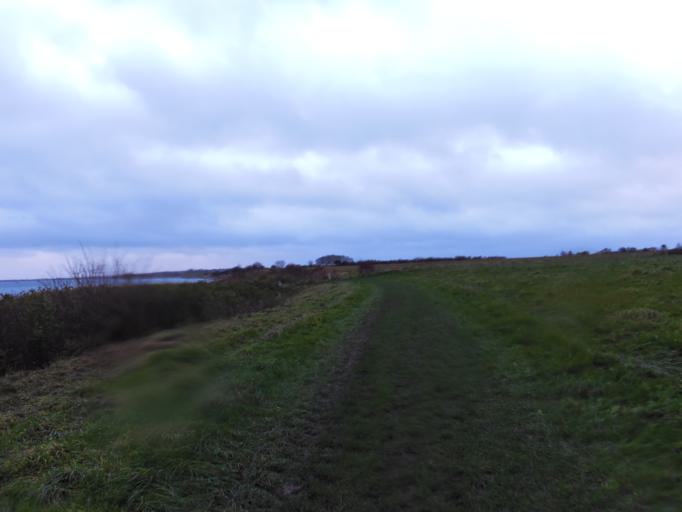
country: DK
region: Central Jutland
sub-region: Arhus Kommune
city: Beder
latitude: 56.0168
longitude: 10.2734
